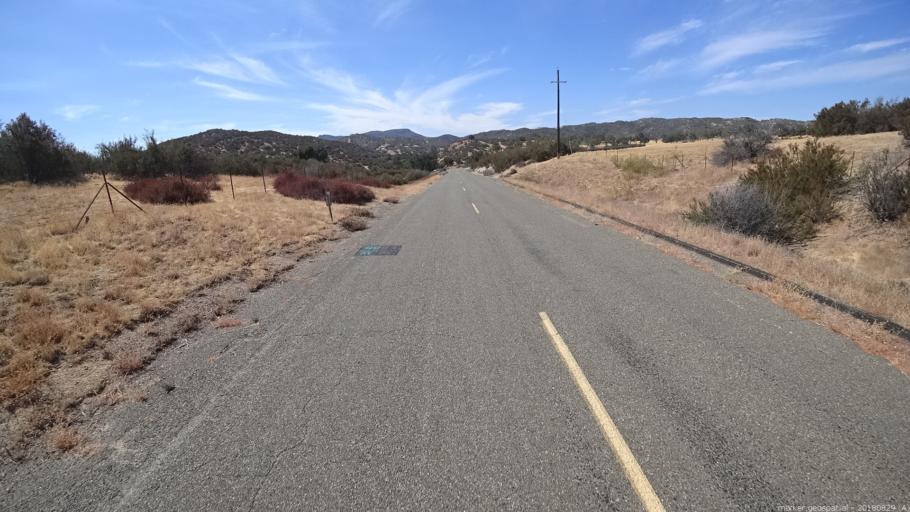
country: US
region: California
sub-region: San Luis Obispo County
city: Lake Nacimiento
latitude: 35.8173
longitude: -120.9800
